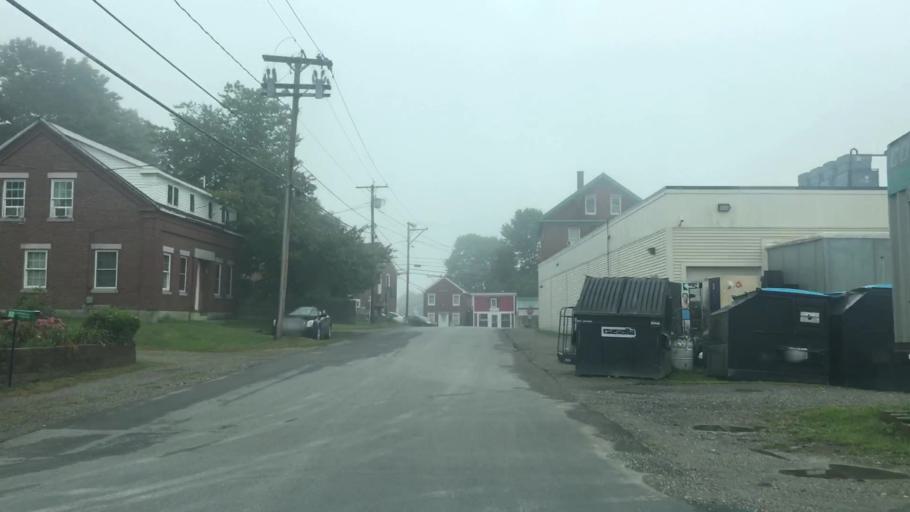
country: US
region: Maine
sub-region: Waldo County
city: Stockton Springs
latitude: 44.4592
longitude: -68.9266
